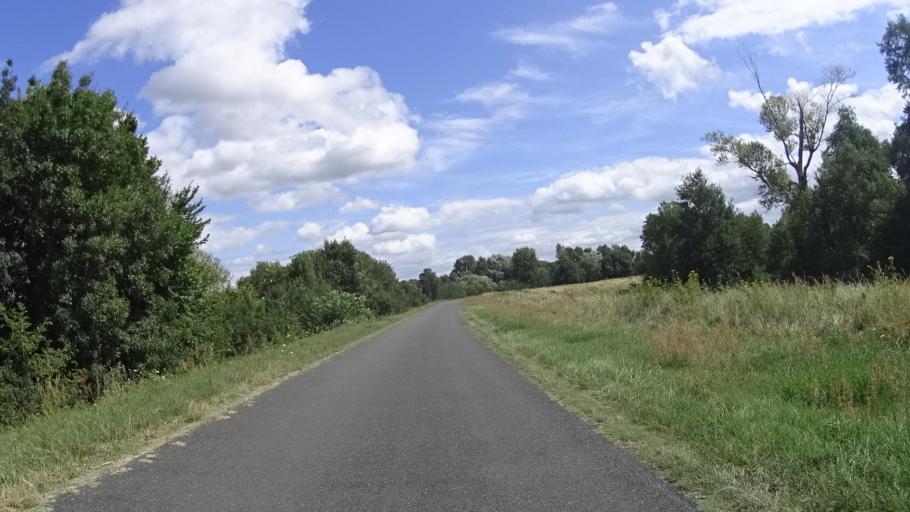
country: FR
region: Centre
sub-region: Departement d'Indre-et-Loire
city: Cinq-Mars-la-Pile
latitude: 47.3410
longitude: 0.4774
